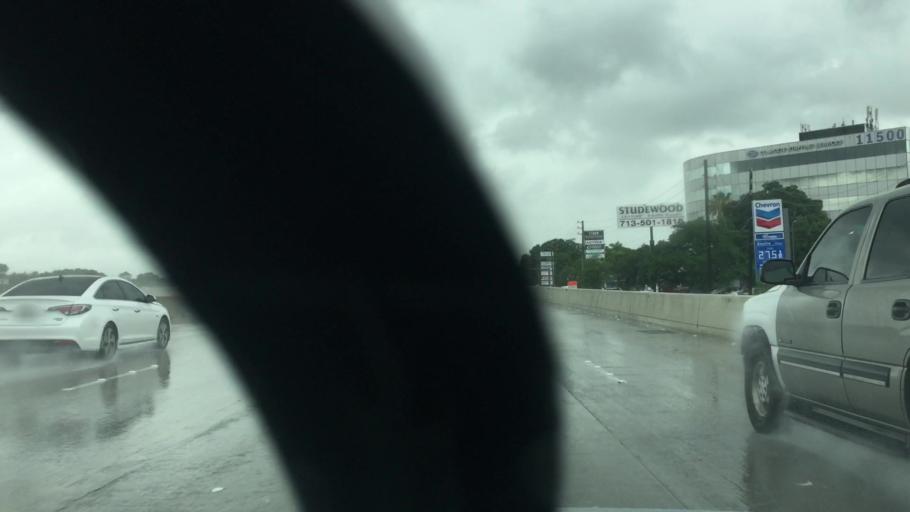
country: US
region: Texas
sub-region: Harris County
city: Spring Valley
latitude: 29.8217
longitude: -95.4707
